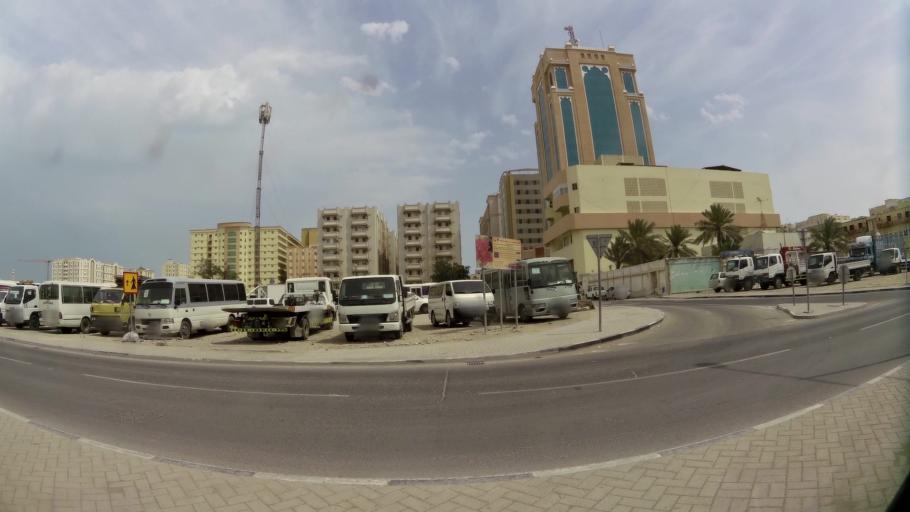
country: QA
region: Baladiyat ad Dawhah
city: Doha
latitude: 25.2757
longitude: 51.5282
